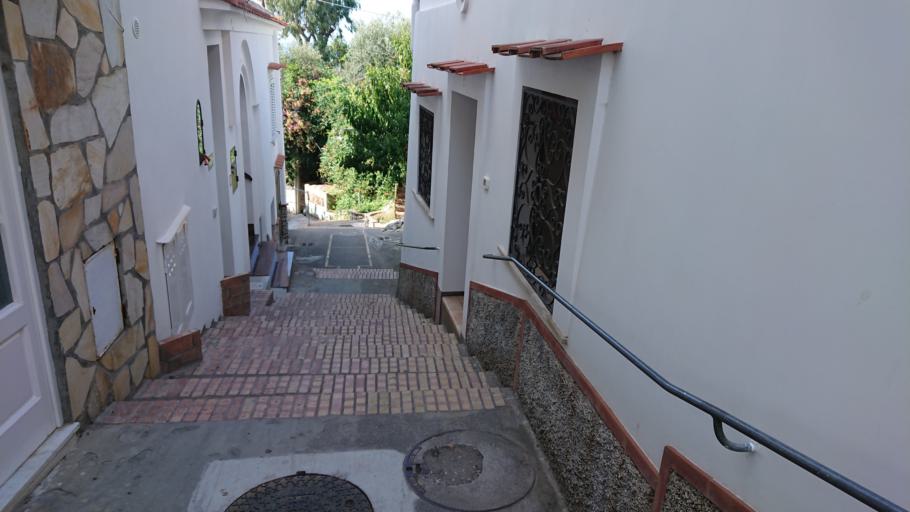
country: IT
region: Campania
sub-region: Provincia di Napoli
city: Anacapri
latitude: 40.5552
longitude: 14.2157
